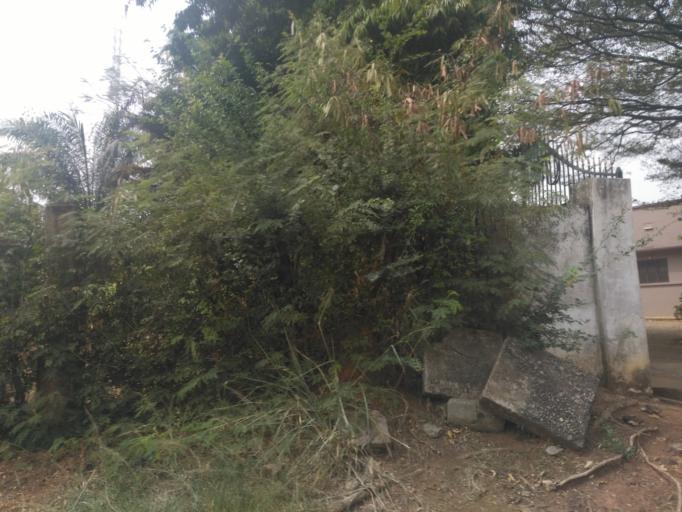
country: GH
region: Ashanti
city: Kumasi
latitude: 6.6755
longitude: -1.6178
